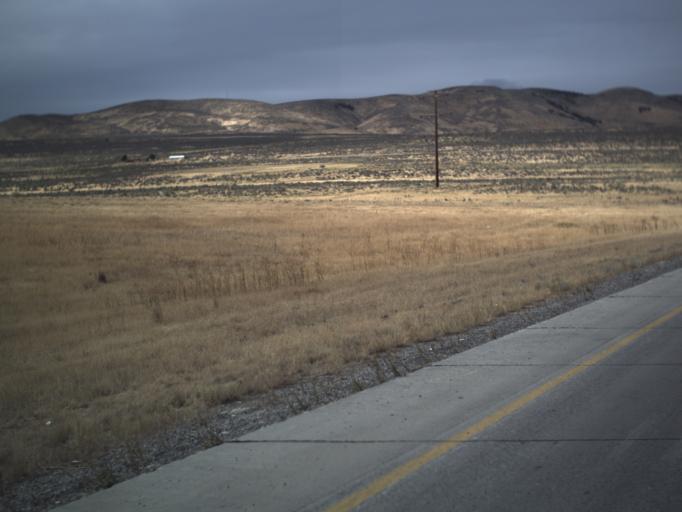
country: US
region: Utah
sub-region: Box Elder County
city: Tremonton
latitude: 41.7269
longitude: -112.1915
